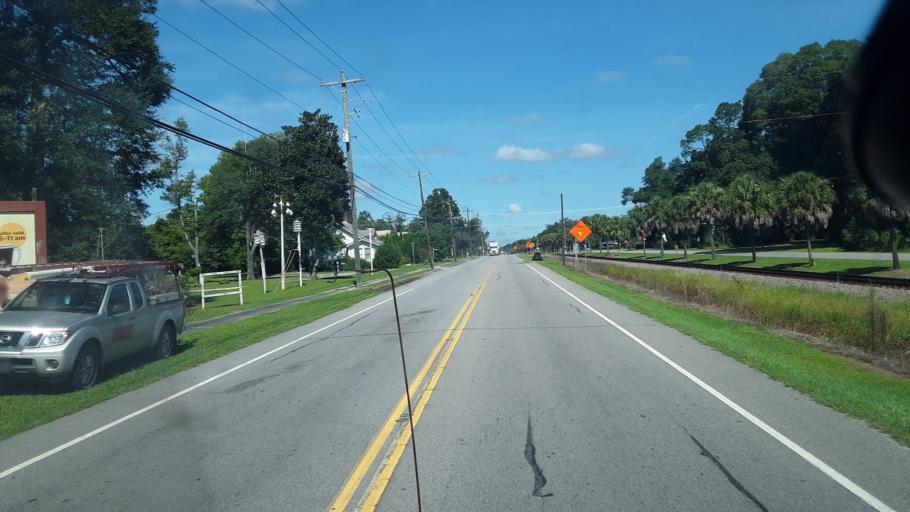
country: US
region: South Carolina
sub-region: Hampton County
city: Varnville
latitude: 32.8453
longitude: -81.0734
